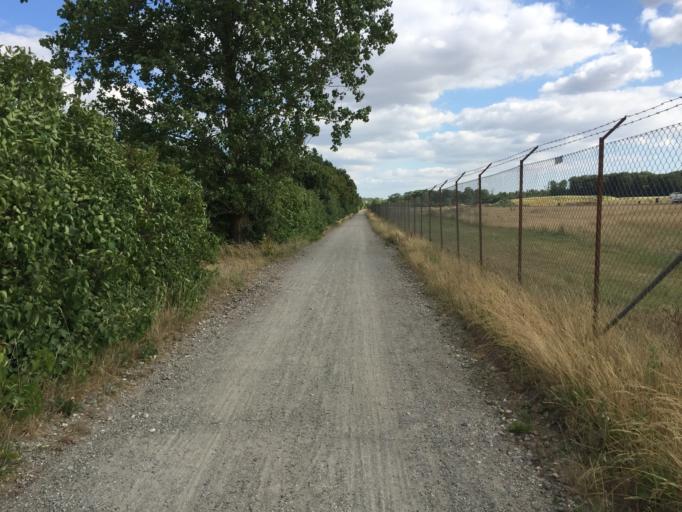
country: DK
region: South Denmark
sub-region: Odense Kommune
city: Neder Holluf
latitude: 55.3629
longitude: 10.4326
